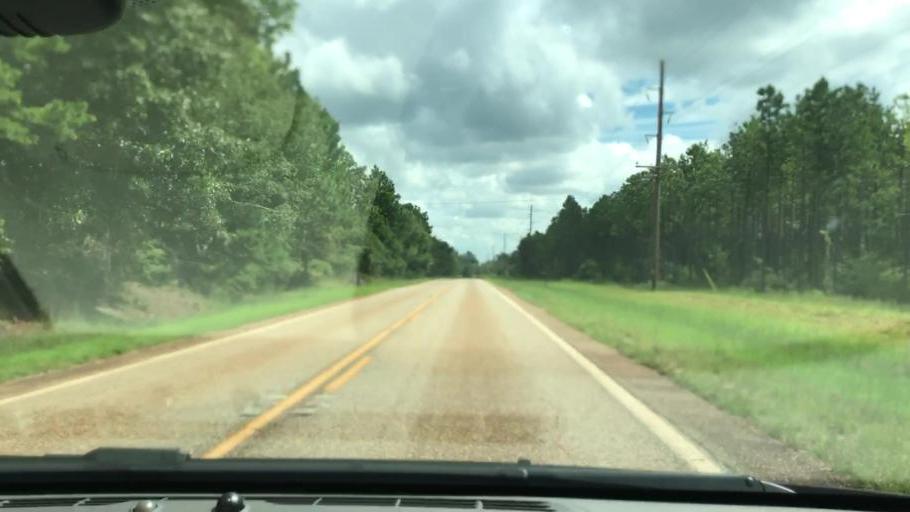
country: US
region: Georgia
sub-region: Stewart County
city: Lumpkin
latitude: 32.0672
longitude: -84.8912
